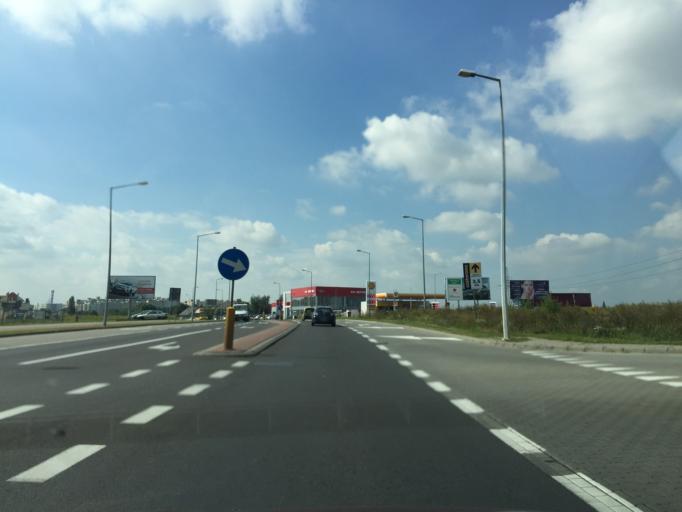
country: PL
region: Greater Poland Voivodeship
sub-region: Kalisz
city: Kalisz
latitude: 51.7630
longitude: 18.0609
